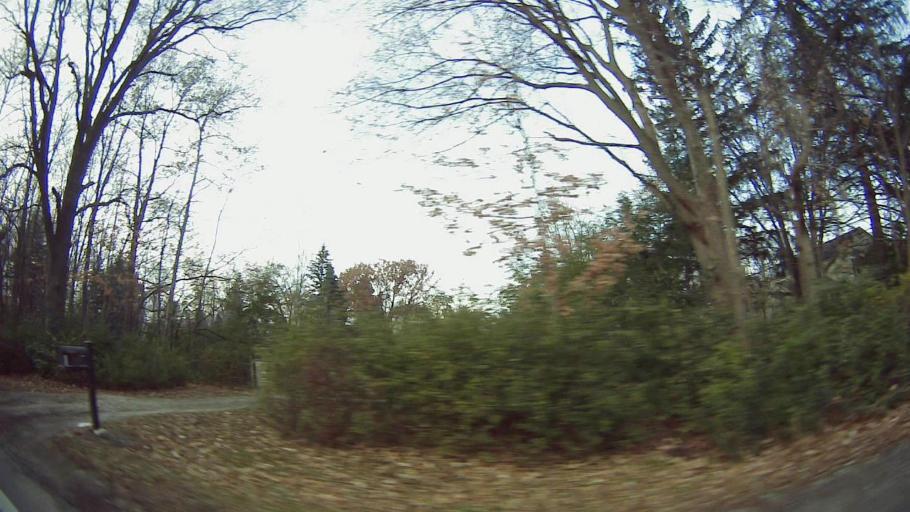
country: US
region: Michigan
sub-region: Oakland County
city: Bingham Farms
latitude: 42.5160
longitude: -83.2690
